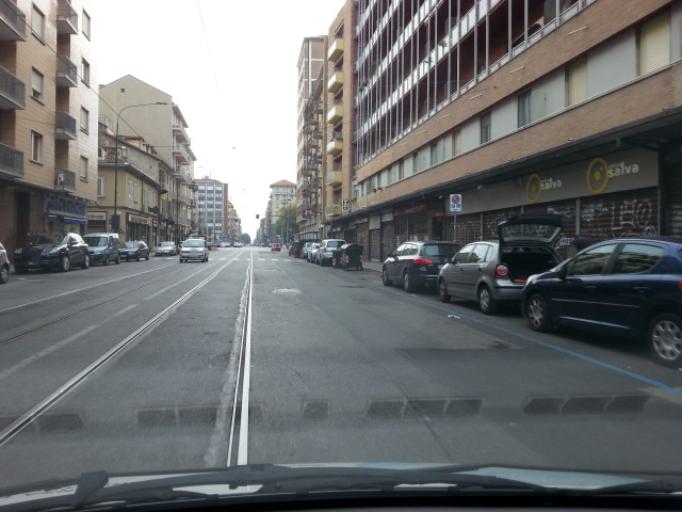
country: IT
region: Piedmont
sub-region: Provincia di Torino
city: Turin
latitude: 45.0486
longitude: 7.6735
